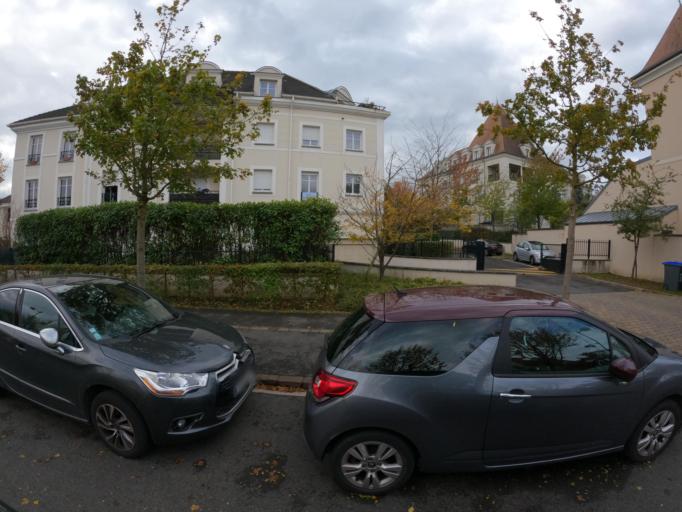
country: FR
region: Ile-de-France
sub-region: Departement de Seine-et-Marne
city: Magny-le-Hongre
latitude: 48.8705
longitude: 2.8137
